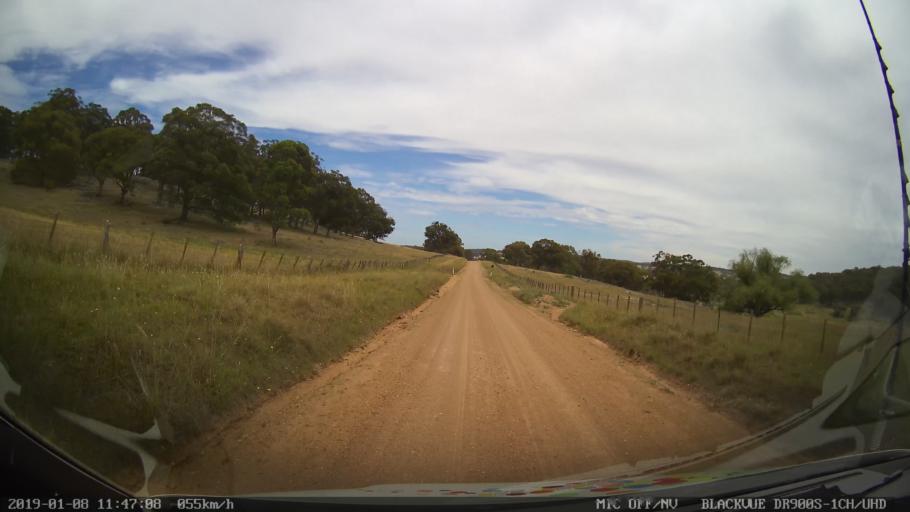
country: AU
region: New South Wales
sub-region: Armidale Dumaresq
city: Armidale
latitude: -30.3787
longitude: 151.5763
